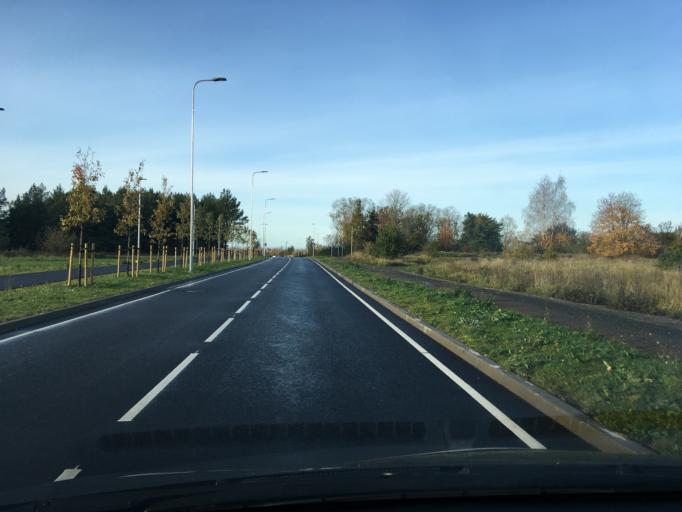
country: EE
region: Harju
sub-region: Viimsi vald
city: Viimsi
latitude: 59.4483
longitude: 24.8231
